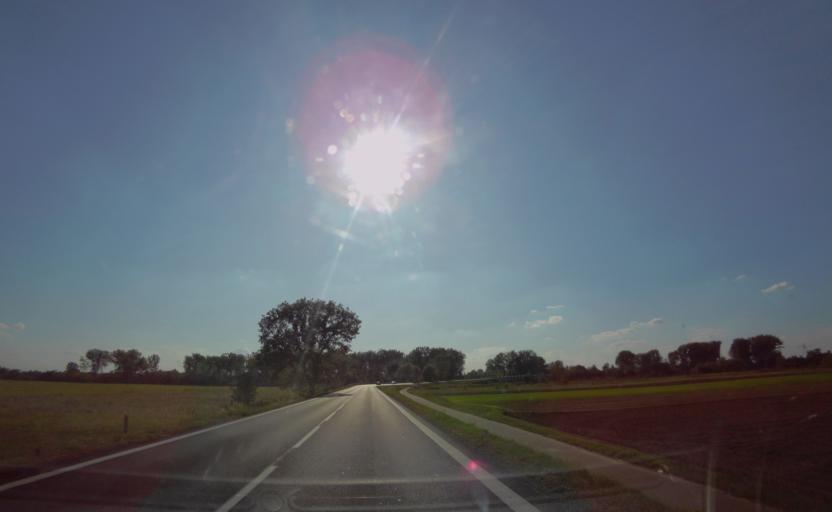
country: PL
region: Subcarpathian Voivodeship
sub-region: Powiat lezajski
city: Stare Miasto
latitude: 50.2923
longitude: 22.4473
